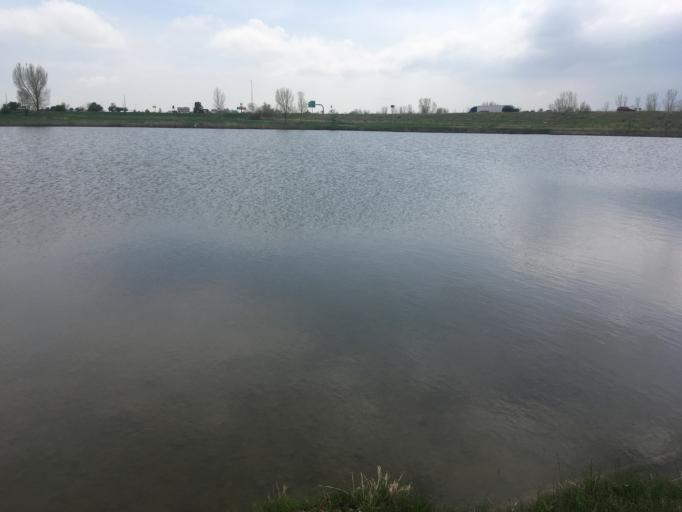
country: US
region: Colorado
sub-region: Weld County
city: Mead
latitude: 40.1700
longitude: -104.9780
